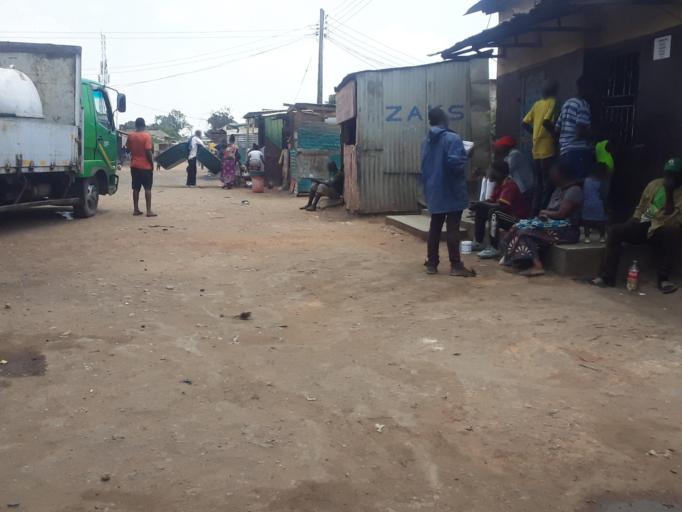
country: ZM
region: Lusaka
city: Lusaka
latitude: -15.3648
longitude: 28.3002
